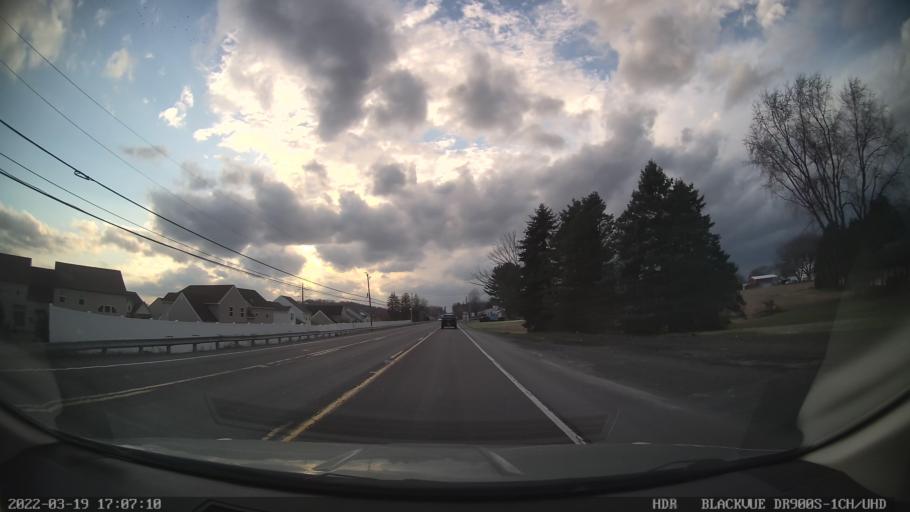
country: US
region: Pennsylvania
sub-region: Lehigh County
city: Breinigsville
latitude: 40.5391
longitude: -75.6394
